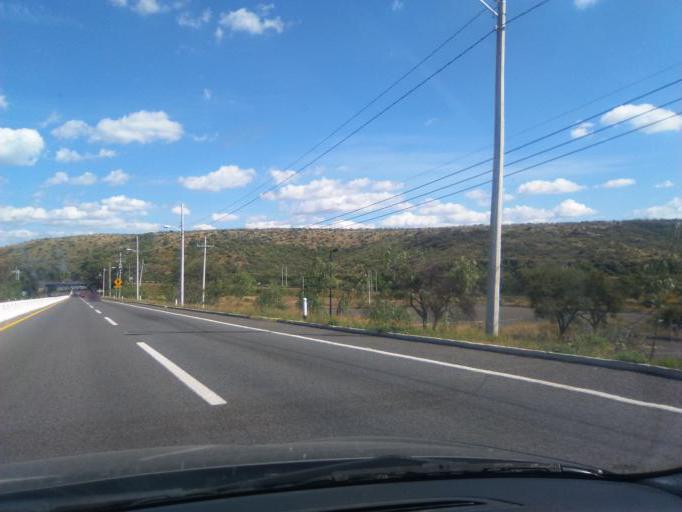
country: MX
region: Guanajuato
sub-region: Silao de la Victoria
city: Aguas Buenas
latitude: 20.9587
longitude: -101.3566
